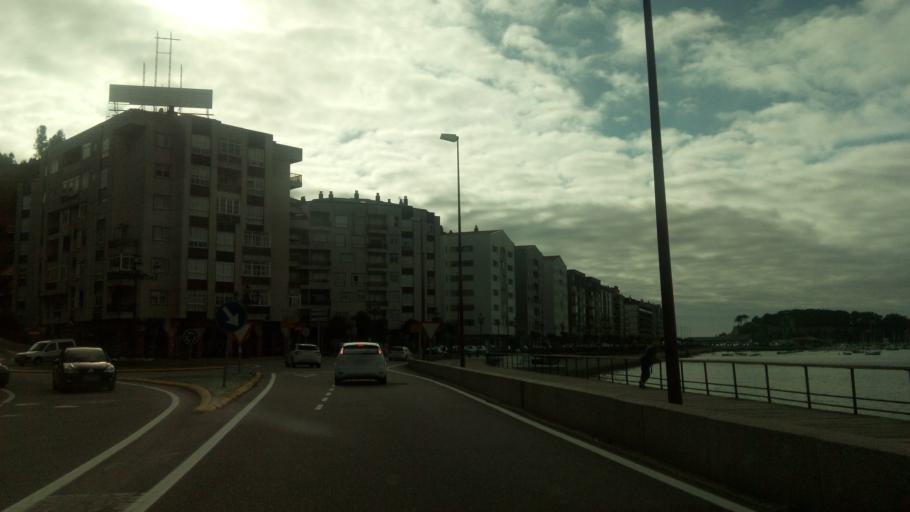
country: ES
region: Galicia
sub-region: Provincia de Pontevedra
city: Baiona
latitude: 42.1143
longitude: -8.8401
